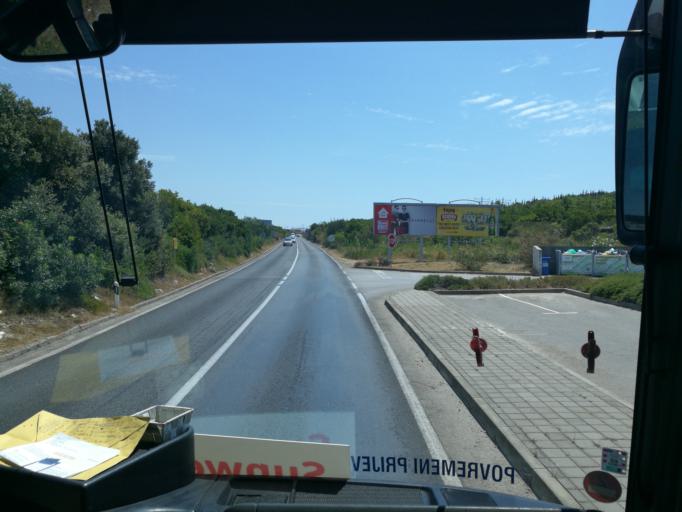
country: HR
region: Dubrovacko-Neretvanska
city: Cavtat
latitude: 42.5734
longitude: 18.2411
